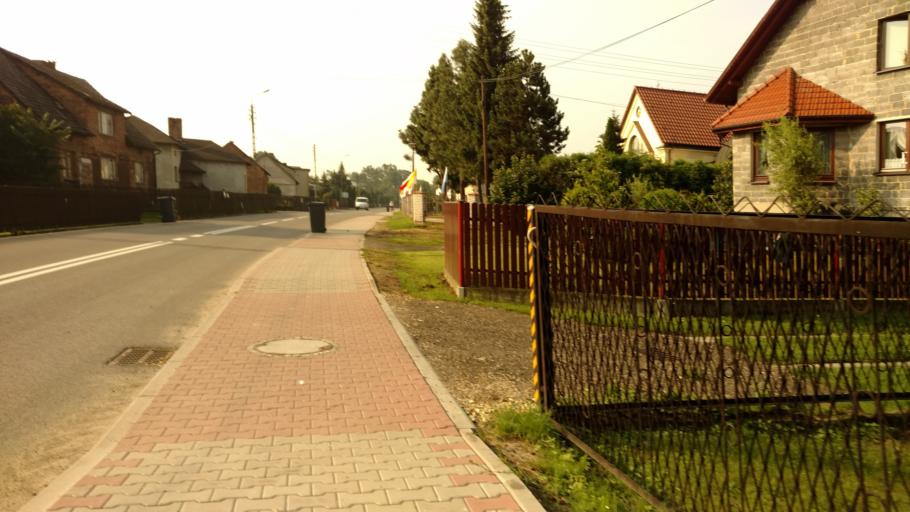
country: PL
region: Silesian Voivodeship
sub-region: Powiat pszczynski
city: Jankowice
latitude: 50.0202
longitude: 18.9821
